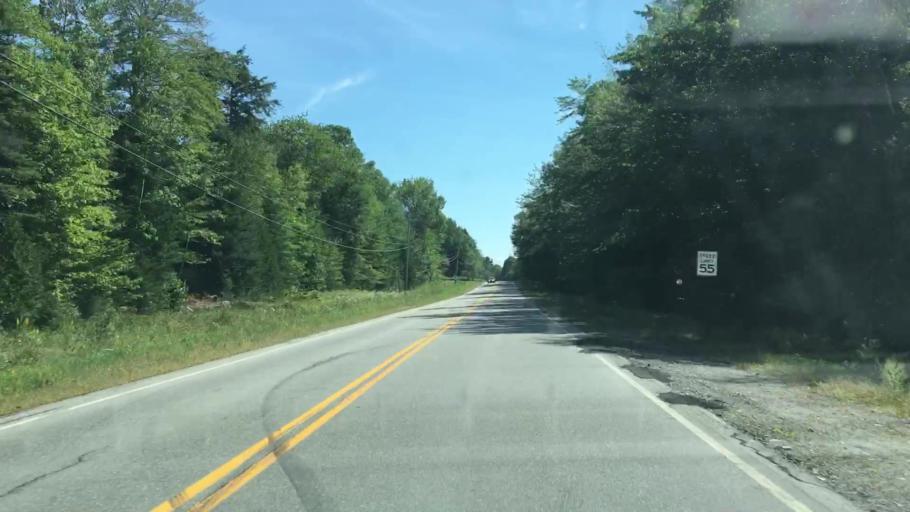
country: US
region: Maine
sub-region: Piscataquis County
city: Milo
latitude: 45.1989
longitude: -68.9055
